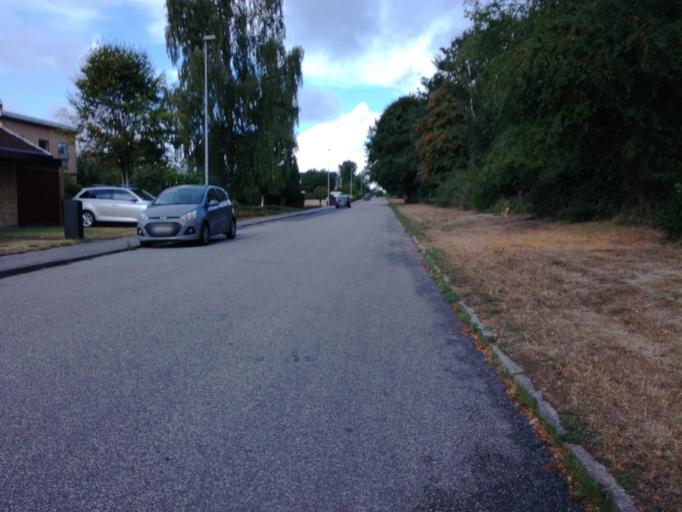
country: DK
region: South Denmark
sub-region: Fredericia Kommune
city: Fredericia
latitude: 55.5830
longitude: 9.7852
